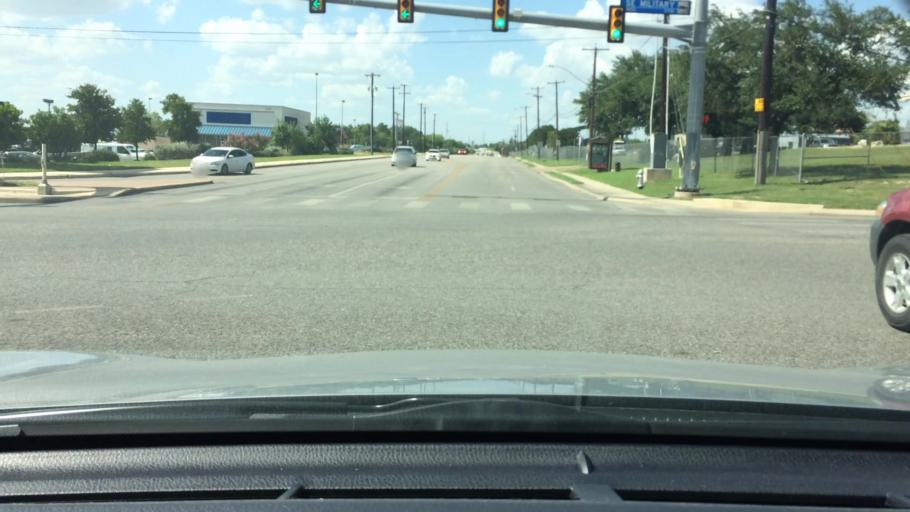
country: US
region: Texas
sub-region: Bexar County
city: San Antonio
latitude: 29.3517
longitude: -98.4484
